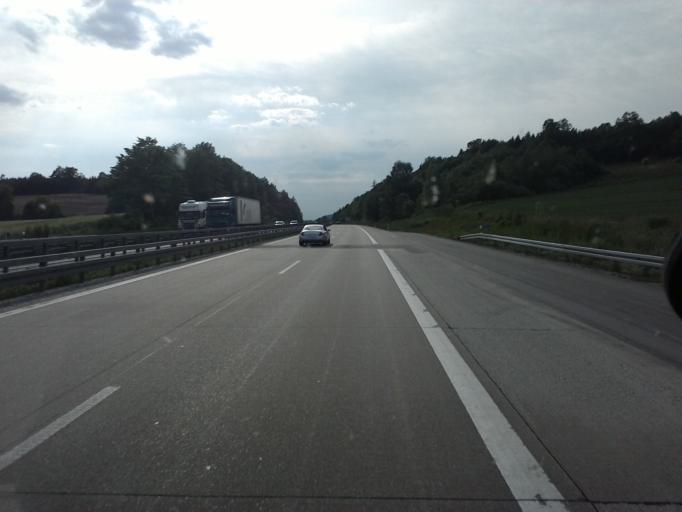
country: DE
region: Bavaria
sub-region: Lower Bavaria
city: Steinach
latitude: 48.9391
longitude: 12.6559
